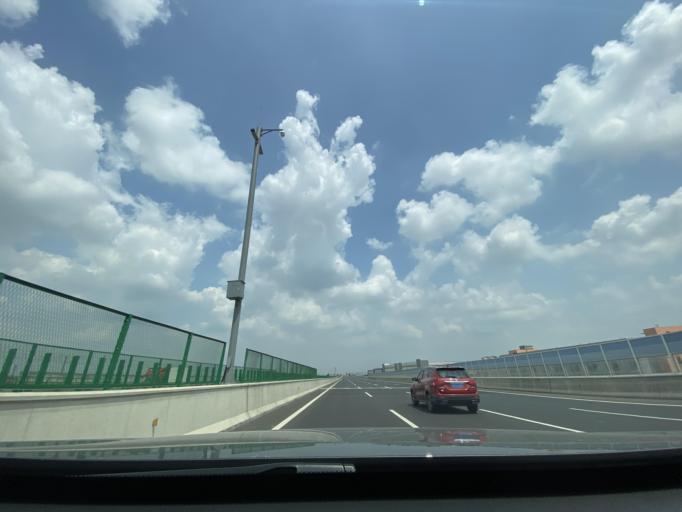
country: CN
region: Sichuan
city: Longquan
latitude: 30.5244
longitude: 104.1710
